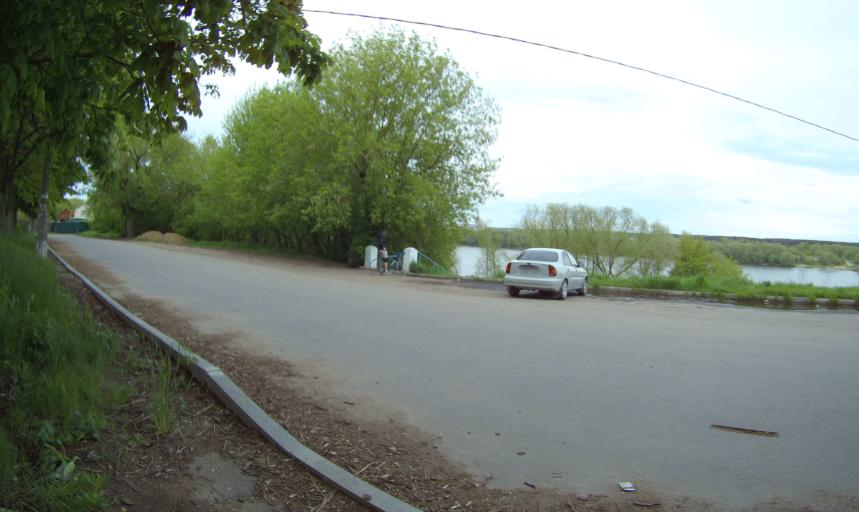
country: RU
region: Moskovskaya
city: Kolomna
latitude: 55.0702
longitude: 38.8052
